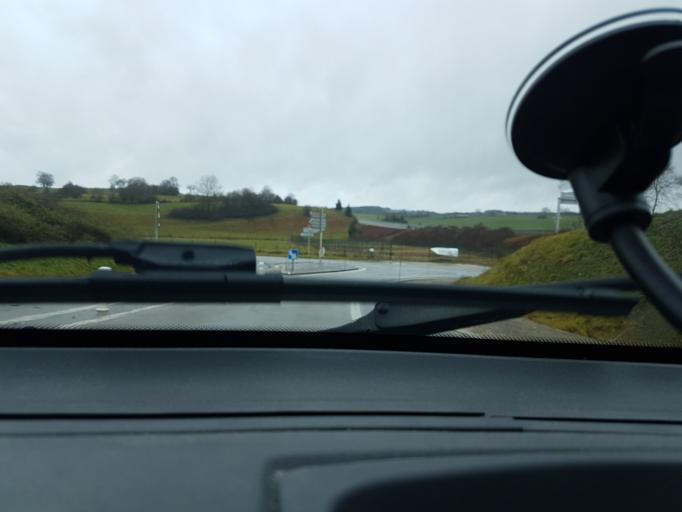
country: FR
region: Franche-Comte
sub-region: Departement du Doubs
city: Vercel-Villedieu-le-Camp
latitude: 47.1447
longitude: 6.4450
